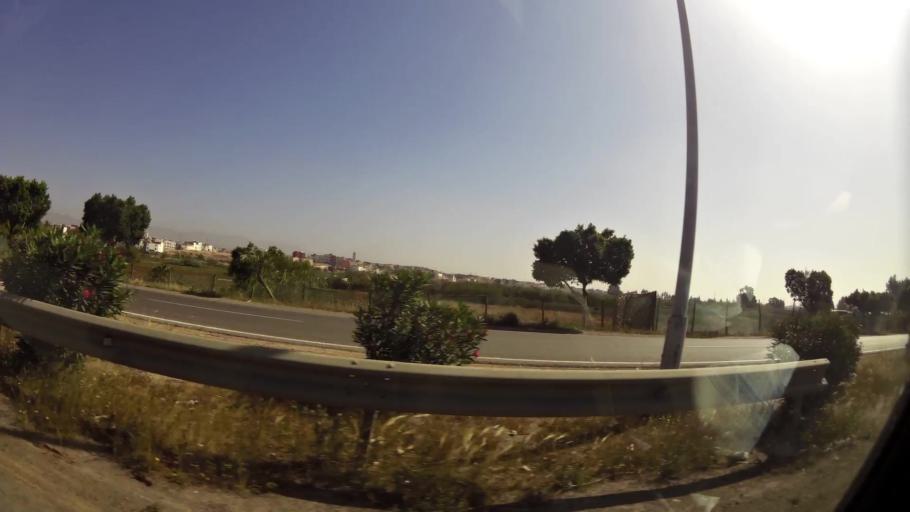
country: MA
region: Souss-Massa-Draa
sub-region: Inezgane-Ait Mellou
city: Inezgane
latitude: 30.3680
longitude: -9.4978
